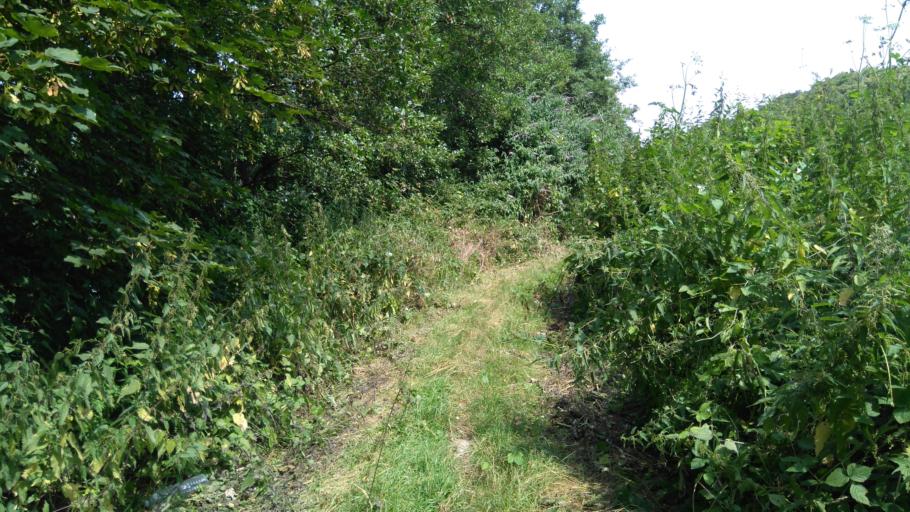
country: FR
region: Picardie
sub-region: Departement de l'Oise
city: Thiverny
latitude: 49.2425
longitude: 2.4533
